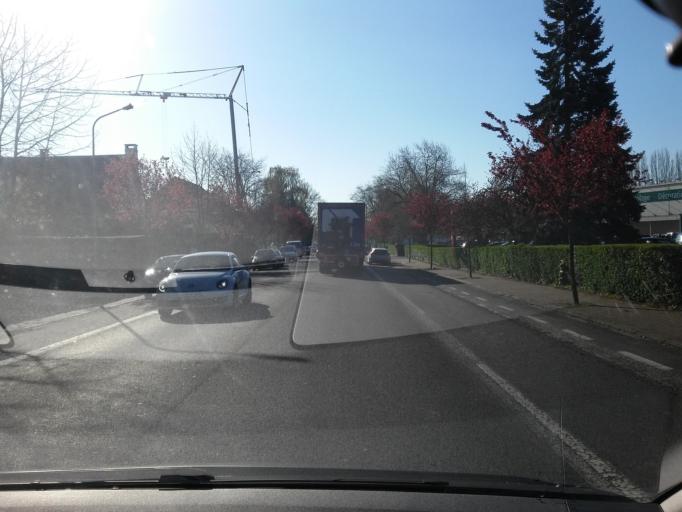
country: BE
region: Wallonia
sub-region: Province du Brabant Wallon
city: Waterloo
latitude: 50.7102
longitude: 4.4040
